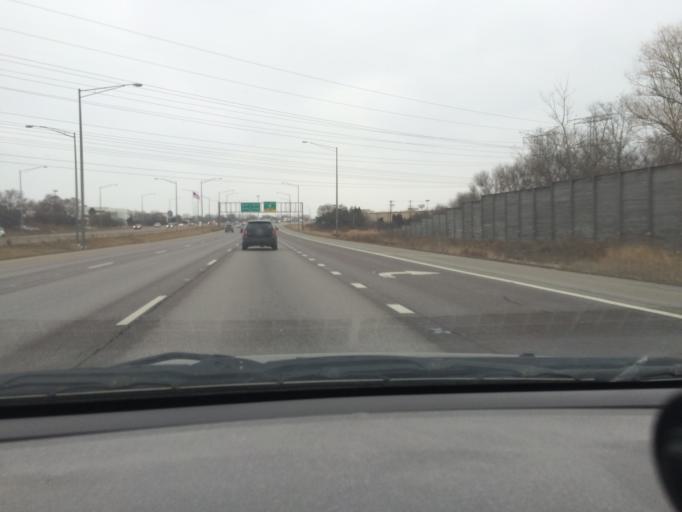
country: US
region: Illinois
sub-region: DuPage County
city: Itasca
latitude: 41.9437
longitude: -88.0373
